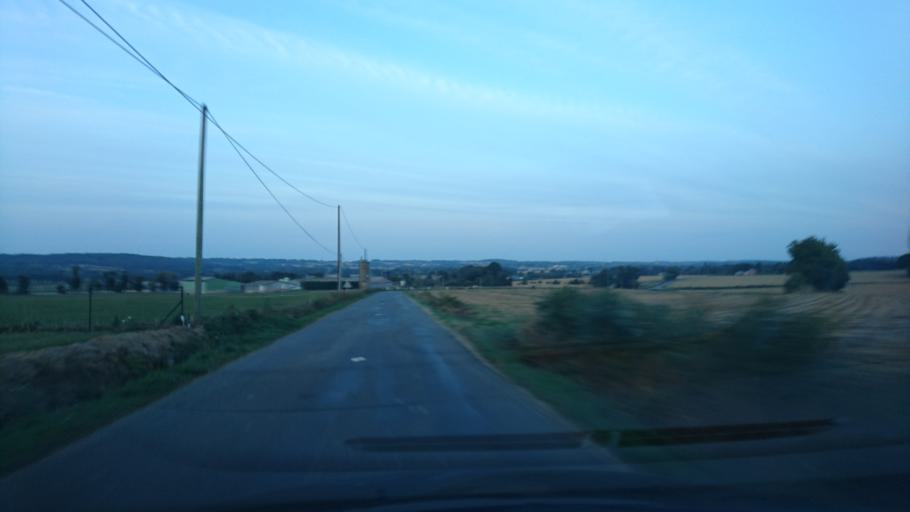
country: FR
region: Brittany
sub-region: Departement d'Ille-et-Vilaine
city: Guignen
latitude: 47.9103
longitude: -1.9107
